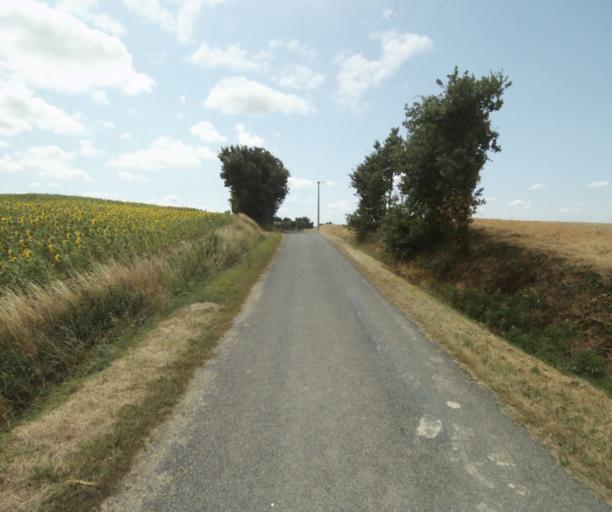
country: FR
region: Midi-Pyrenees
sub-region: Departement de la Haute-Garonne
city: Saint-Felix-Lauragais
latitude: 43.4098
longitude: 1.9049
